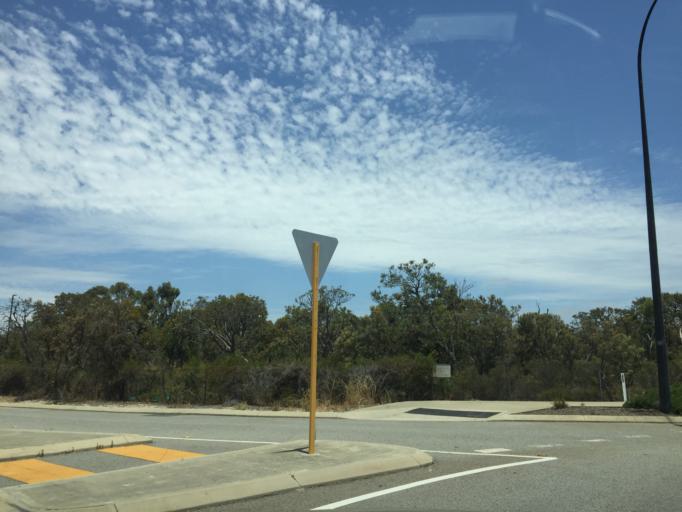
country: AU
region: Western Australia
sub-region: Melville
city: Winthrop
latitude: -32.0734
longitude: 115.8451
